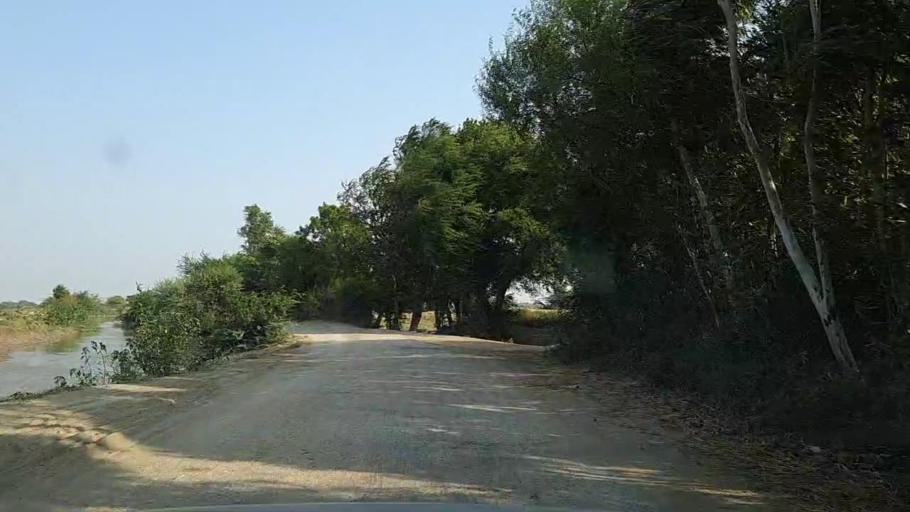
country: PK
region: Sindh
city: Mirpur Sakro
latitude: 24.5969
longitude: 67.5916
